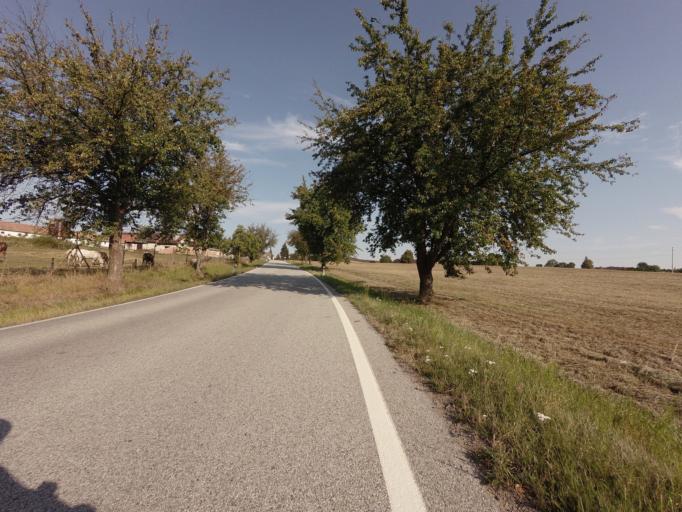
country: CZ
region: Jihocesky
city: Tyn nad Vltavou
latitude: 49.2761
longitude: 14.4014
